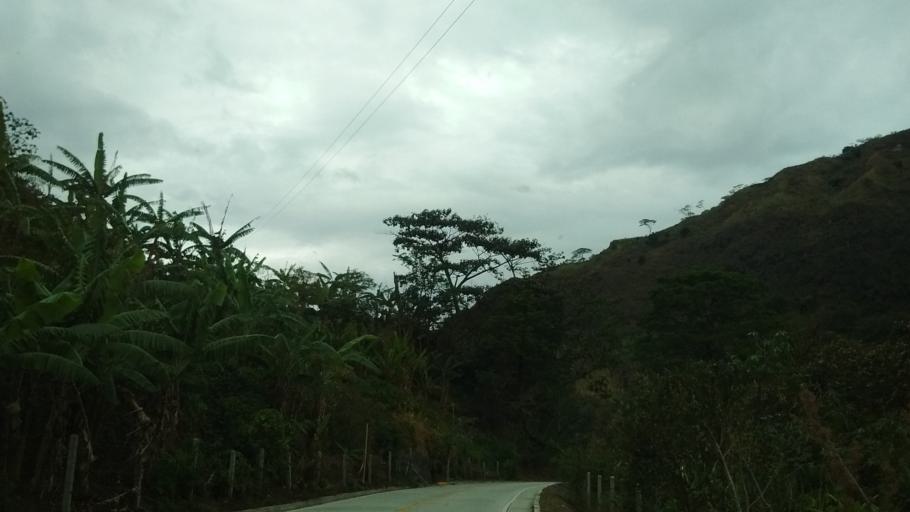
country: CO
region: Cauca
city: La Sierra
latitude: 2.1502
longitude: -76.7649
